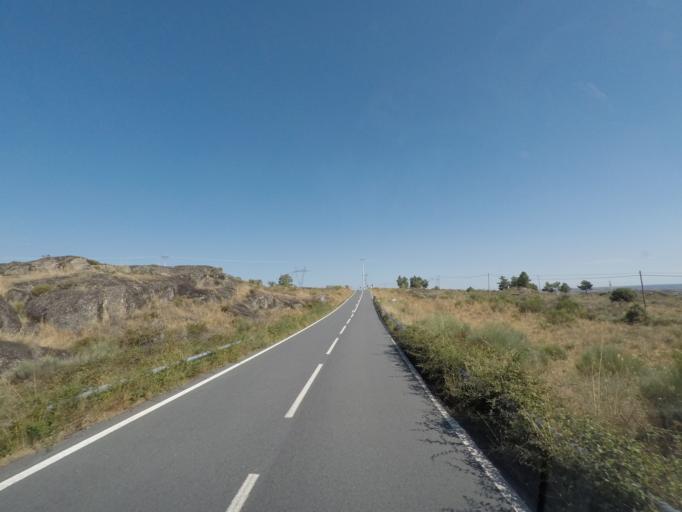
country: ES
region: Castille and Leon
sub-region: Provincia de Salamanca
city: Villarino de los Aires
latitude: 41.3307
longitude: -6.4905
